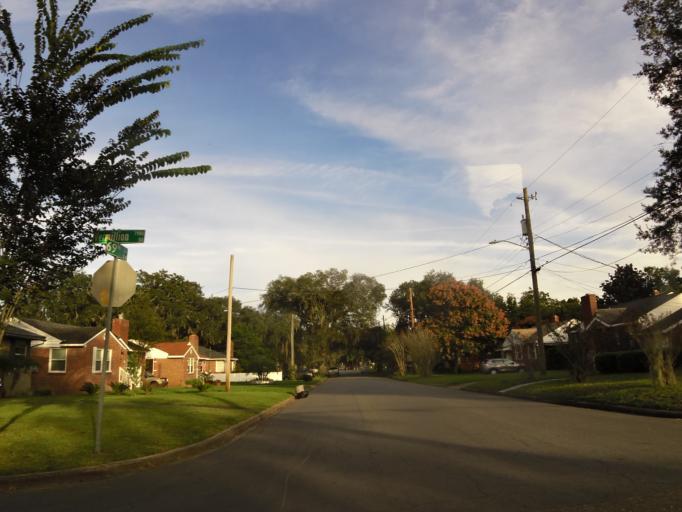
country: US
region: Florida
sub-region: Duval County
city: Jacksonville
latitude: 30.3897
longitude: -81.6588
